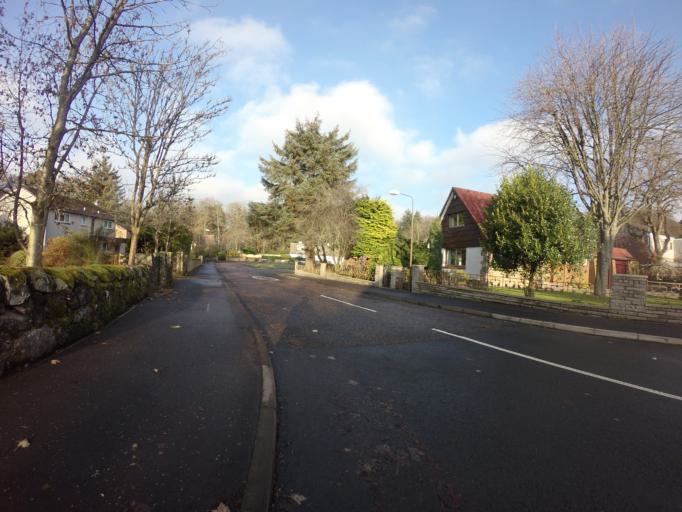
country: GB
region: Scotland
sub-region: West Lothian
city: Livingston
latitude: 55.9099
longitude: -3.5579
